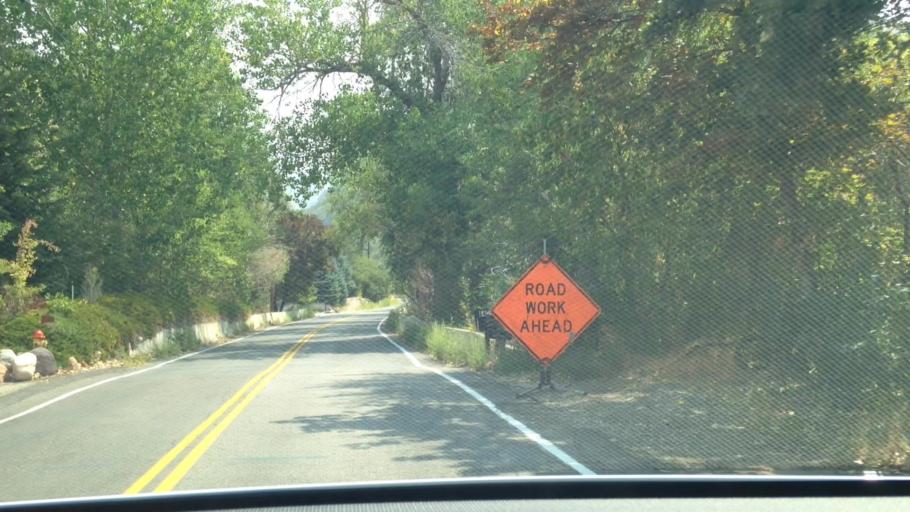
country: US
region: Utah
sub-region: Salt Lake County
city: Mount Olympus
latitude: 40.6892
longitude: -111.7889
